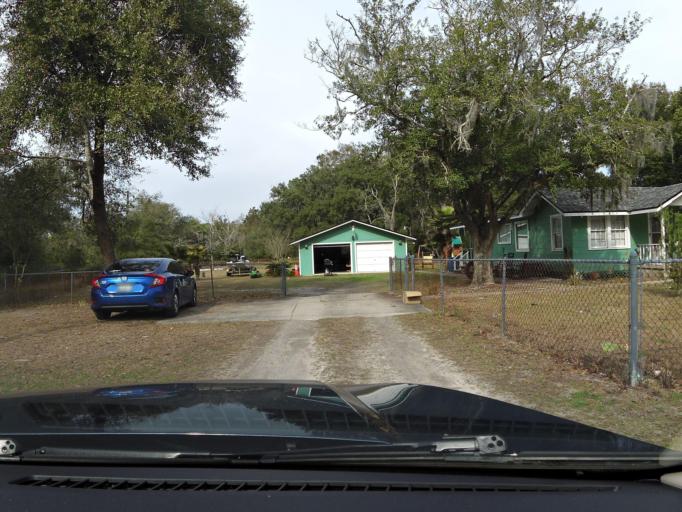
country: US
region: Florida
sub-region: Duval County
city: Jacksonville
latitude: 30.4411
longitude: -81.5995
